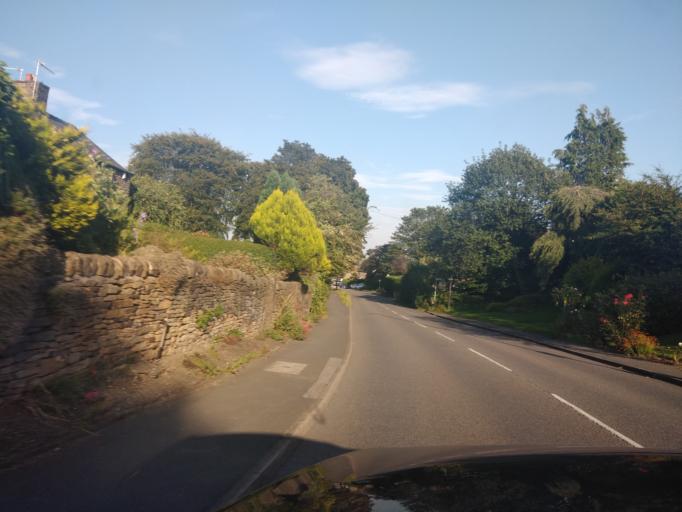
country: GB
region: England
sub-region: Derbyshire
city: Dronfield
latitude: 53.3027
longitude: -1.5045
